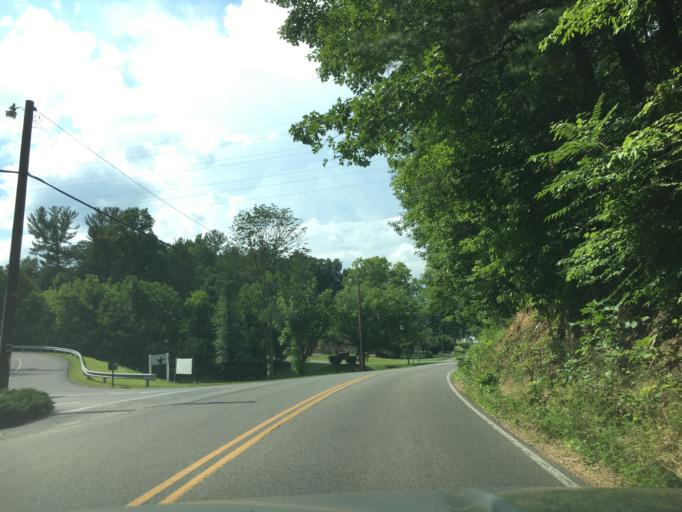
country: US
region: Virginia
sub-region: Roanoke County
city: Cave Spring
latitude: 37.2052
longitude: -80.0082
